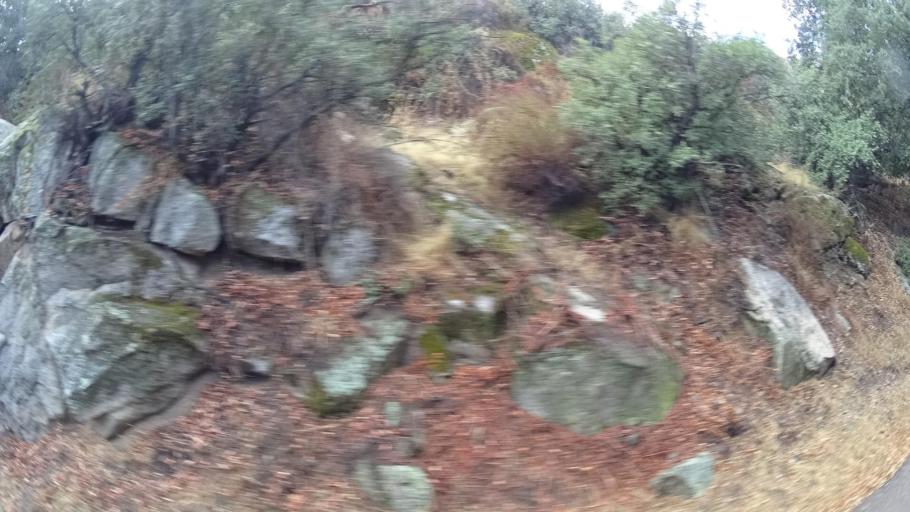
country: US
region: California
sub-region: San Diego County
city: Campo
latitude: 32.6072
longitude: -116.4776
